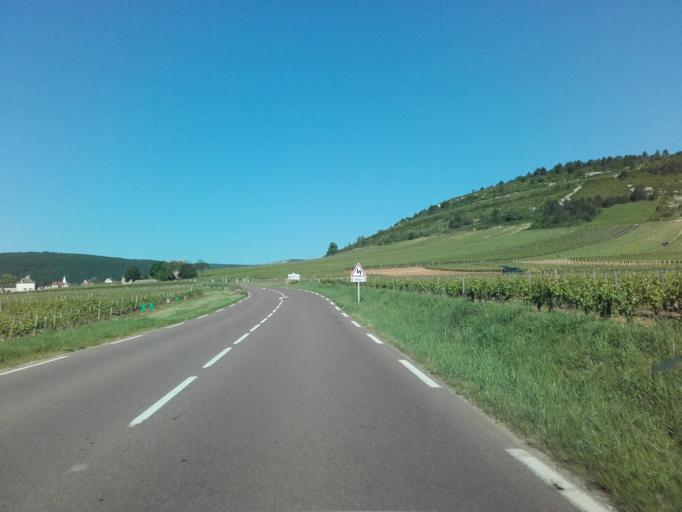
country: FR
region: Bourgogne
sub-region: Departement de la Cote-d'Or
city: Meursault
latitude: 46.9887
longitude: 4.7602
